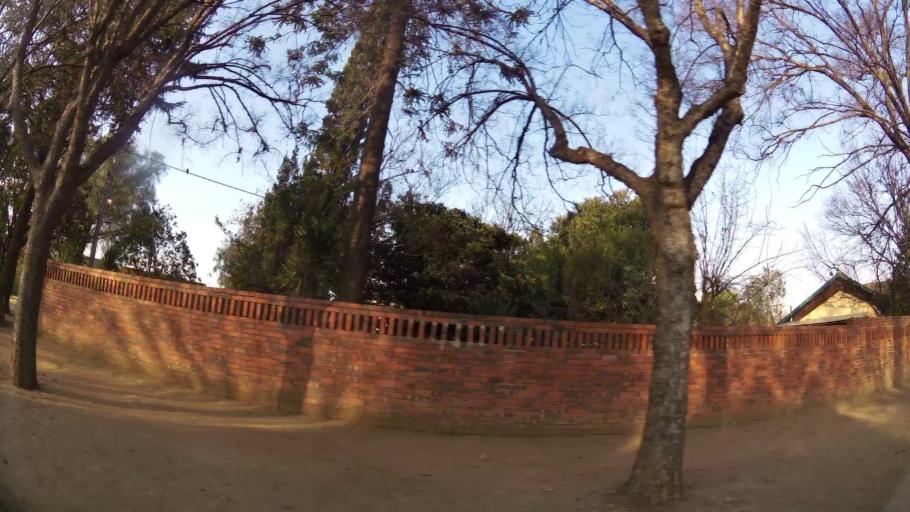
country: ZA
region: Gauteng
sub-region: Ekurhuleni Metropolitan Municipality
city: Springs
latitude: -26.2962
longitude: 28.4472
